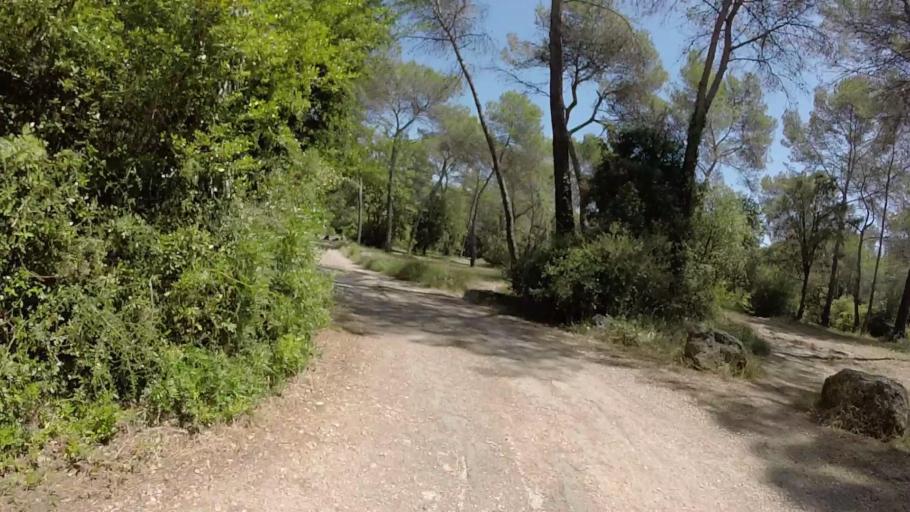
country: FR
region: Provence-Alpes-Cote d'Azur
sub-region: Departement des Alpes-Maritimes
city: Mougins
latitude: 43.5978
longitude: 7.0170
